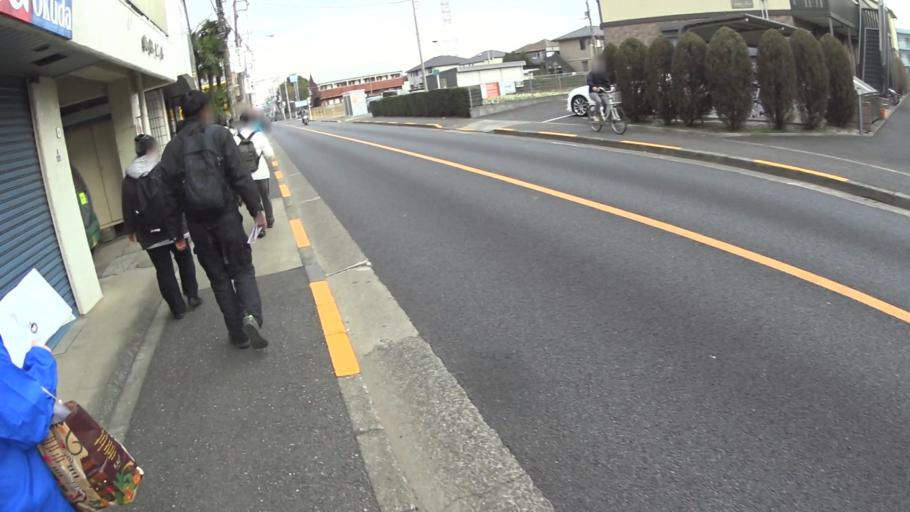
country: JP
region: Tokyo
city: Mitaka-shi
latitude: 35.6729
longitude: 139.5821
